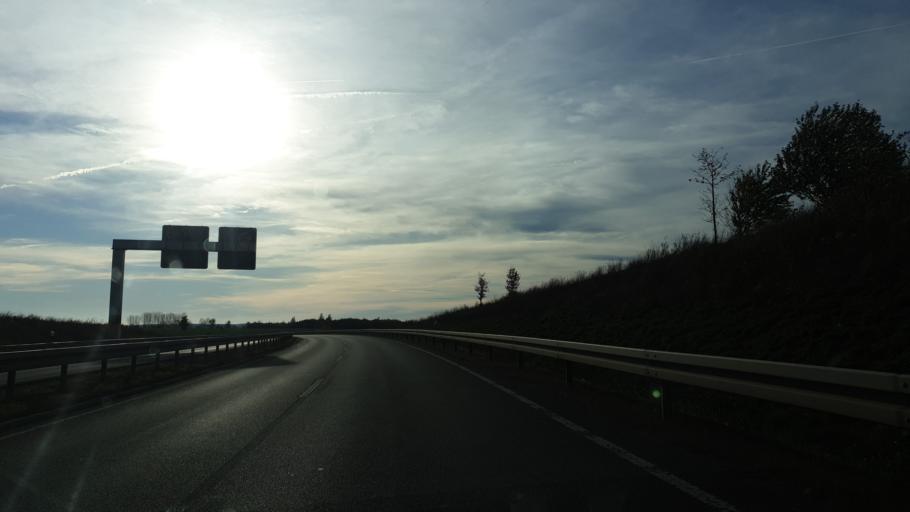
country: DE
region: Thuringia
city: Schwaara
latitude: 50.8958
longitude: 12.1162
